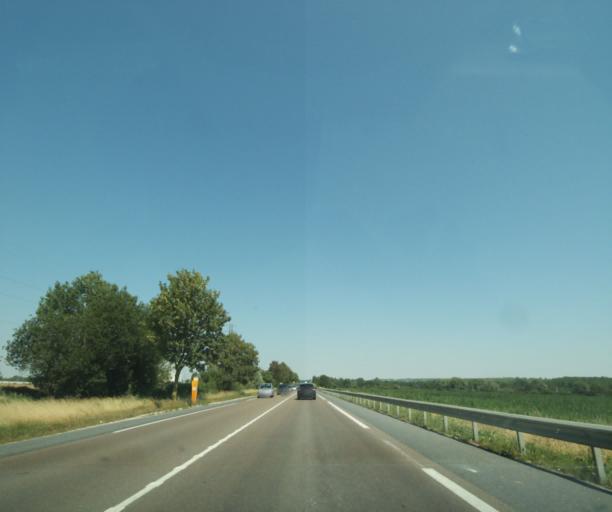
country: FR
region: Champagne-Ardenne
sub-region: Departement de la Marne
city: Frignicourt
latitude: 48.7190
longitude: 4.6320
